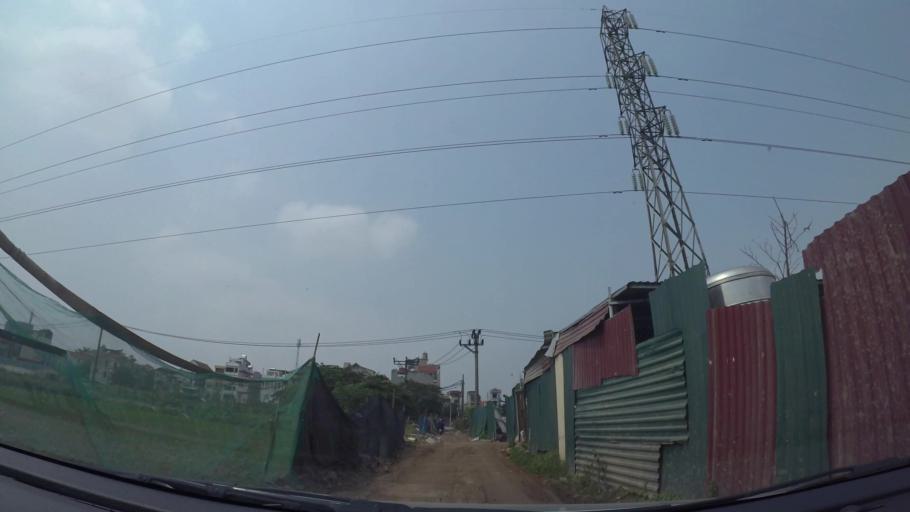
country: VN
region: Ha Noi
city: Tay Ho
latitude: 21.0857
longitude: 105.8002
